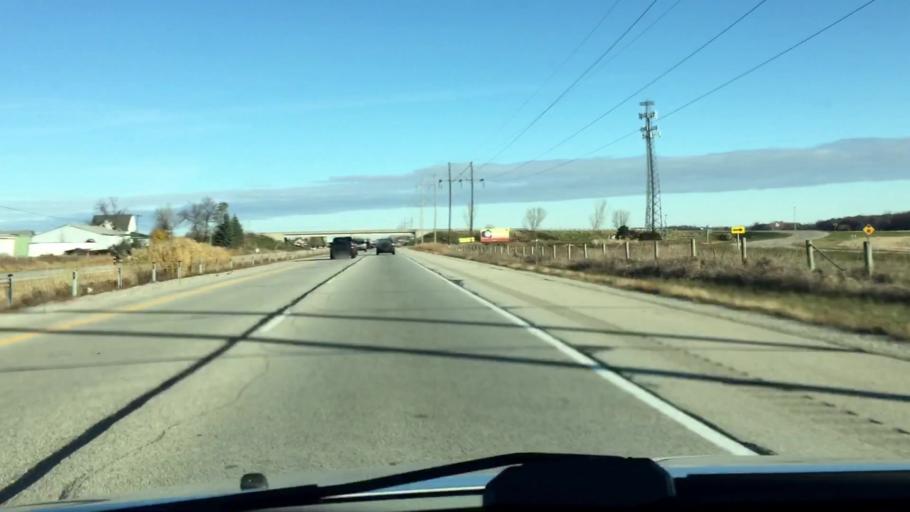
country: US
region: Wisconsin
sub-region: Winnebago County
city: Oshkosh
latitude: 43.9057
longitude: -88.5835
